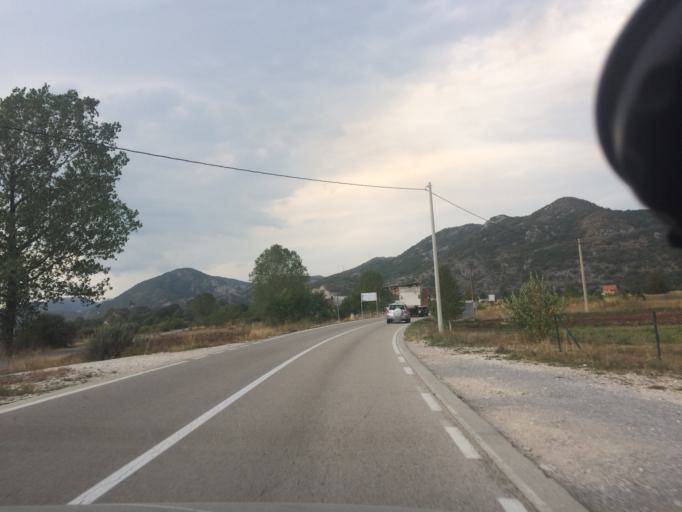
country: ME
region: Kotor
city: Risan
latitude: 42.6469
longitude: 18.6800
